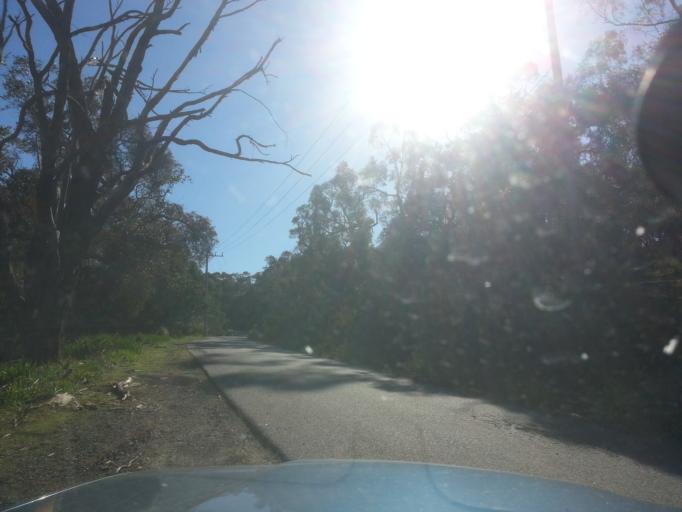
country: AU
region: Victoria
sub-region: Cardinia
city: Beaconsfield Upper
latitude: -37.9693
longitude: 145.3879
